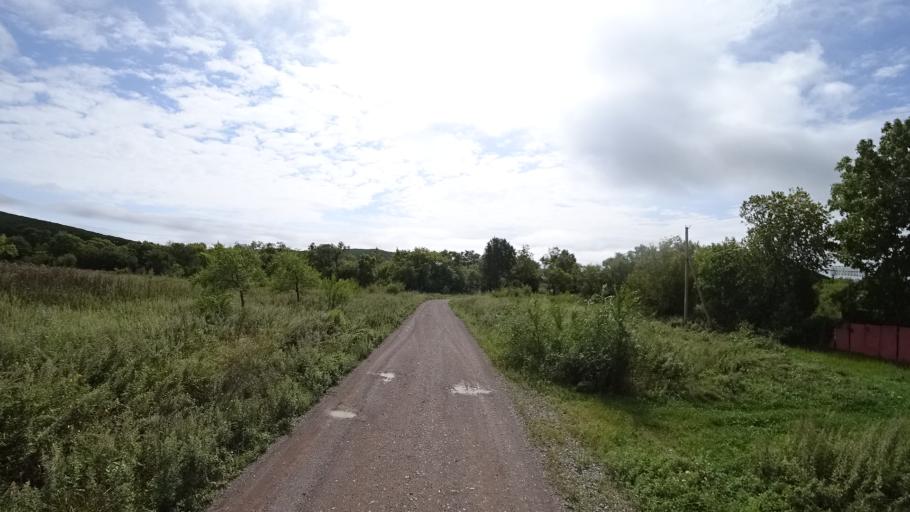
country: RU
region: Primorskiy
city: Lyalichi
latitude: 44.1395
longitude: 132.3752
